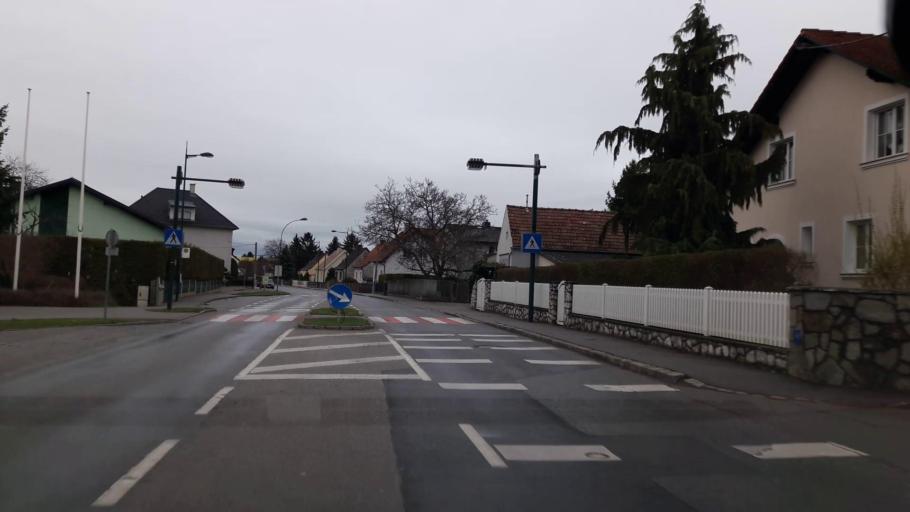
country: AT
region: Lower Austria
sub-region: Politischer Bezirk Bruck an der Leitha
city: Bruck an der Leitha
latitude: 48.0313
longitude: 16.7707
